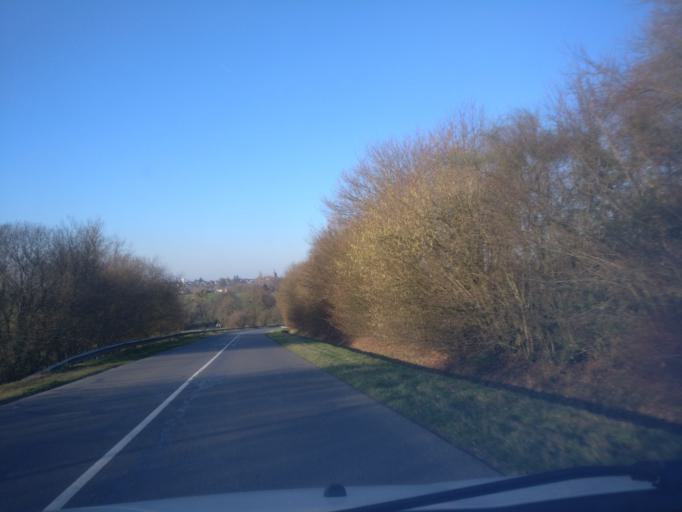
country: FR
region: Brittany
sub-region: Departement d'Ille-et-Vilaine
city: Livre-sur-Changeon
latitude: 48.2083
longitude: -1.3366
